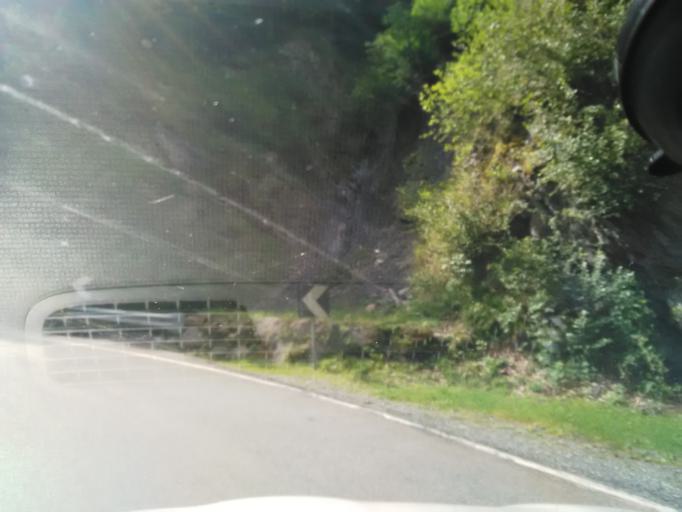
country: IT
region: Piedmont
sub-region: Provincia di Vercelli
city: Fobello
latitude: 45.8887
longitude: 8.1561
